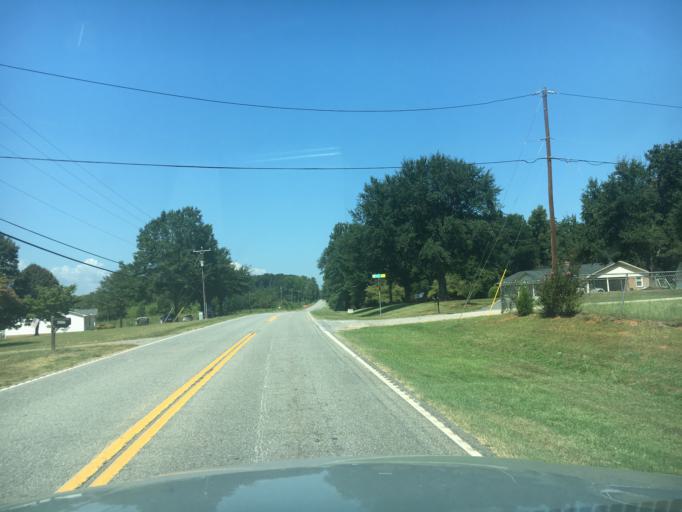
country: US
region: South Carolina
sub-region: Spartanburg County
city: Boiling Springs
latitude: 35.1253
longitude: -82.0310
